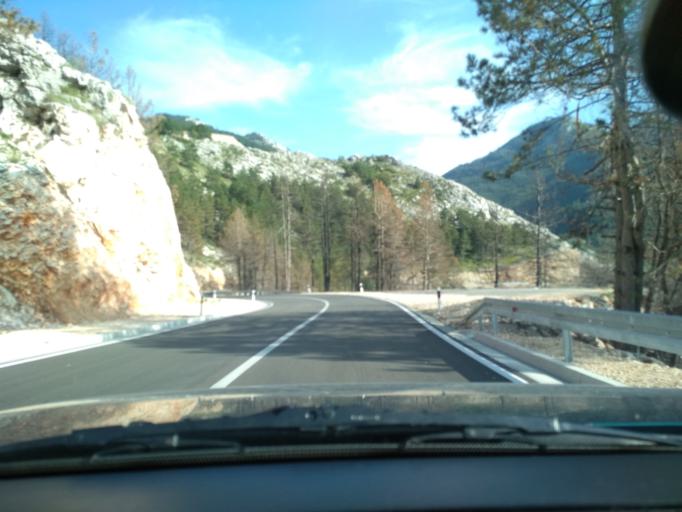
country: ME
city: Dobrota
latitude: 42.4379
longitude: 18.8402
